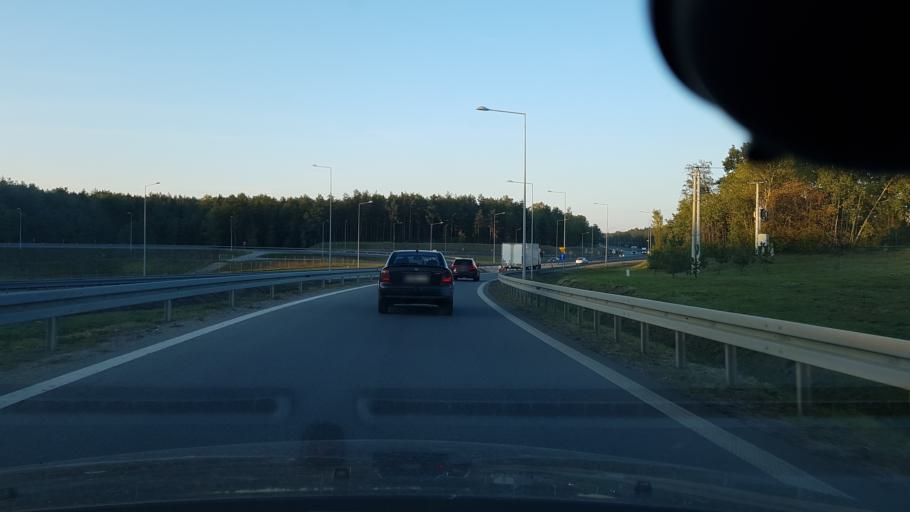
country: PL
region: Lodz Voivodeship
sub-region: Powiat tomaszowski
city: Tomaszow Mazowiecki
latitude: 51.5647
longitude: 20.0221
